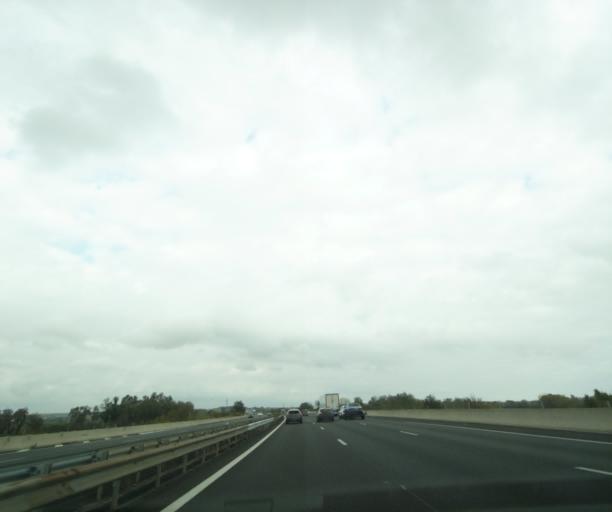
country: FR
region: Languedoc-Roussillon
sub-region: Departement de l'Herault
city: Florensac
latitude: 43.3809
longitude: 3.4478
